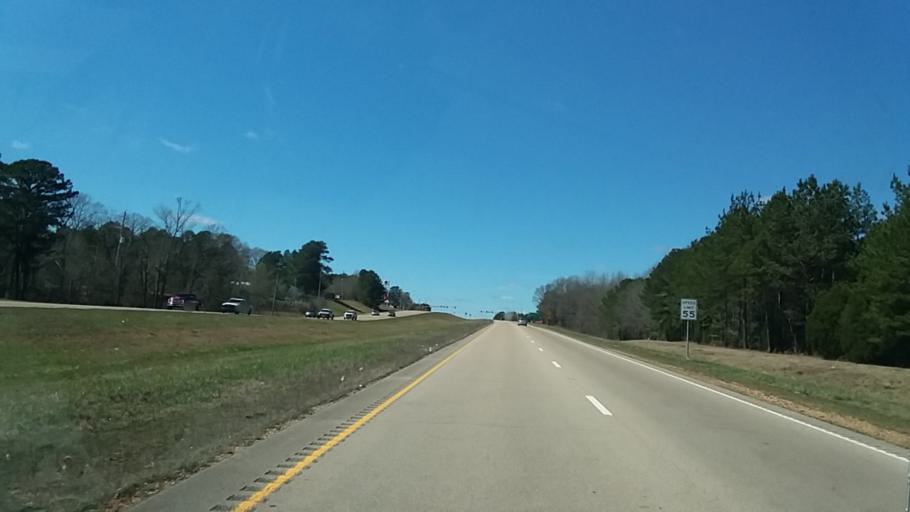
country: US
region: Mississippi
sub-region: Alcorn County
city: Farmington
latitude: 34.8761
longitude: -88.4363
